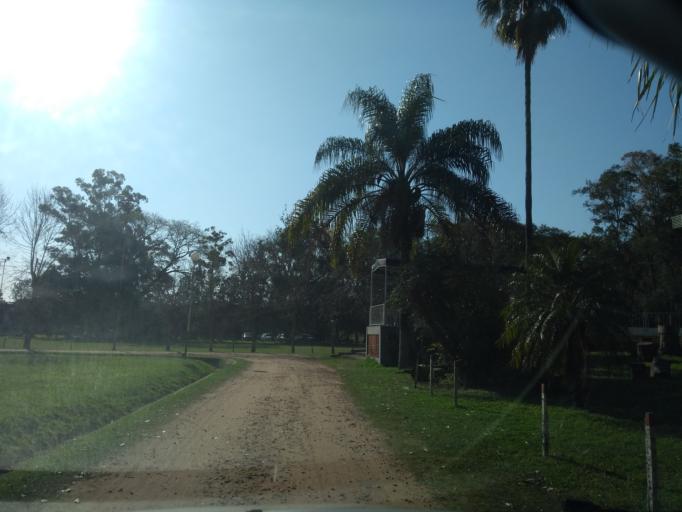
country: AR
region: Chaco
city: Resistencia
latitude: -27.4233
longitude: -58.9476
